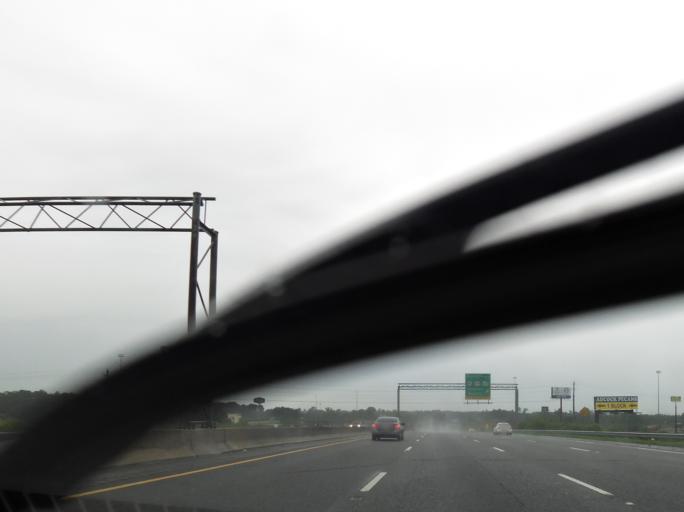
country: US
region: Georgia
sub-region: Tift County
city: Tifton
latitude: 31.4515
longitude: -83.5307
